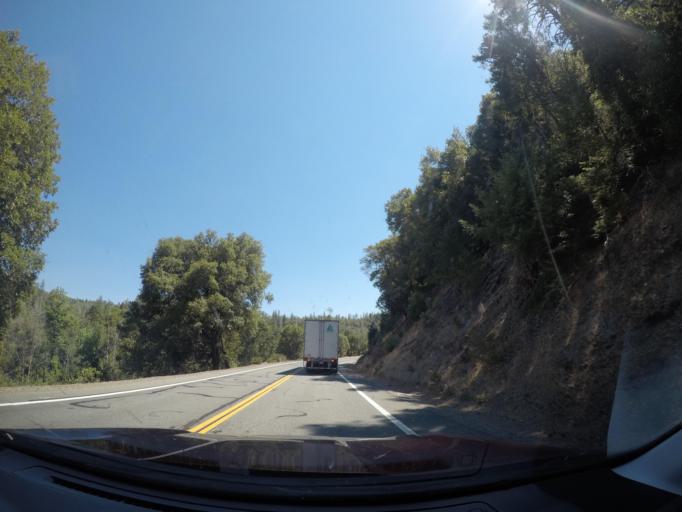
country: US
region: California
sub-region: Shasta County
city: Bella Vista
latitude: 40.7140
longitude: -122.0838
